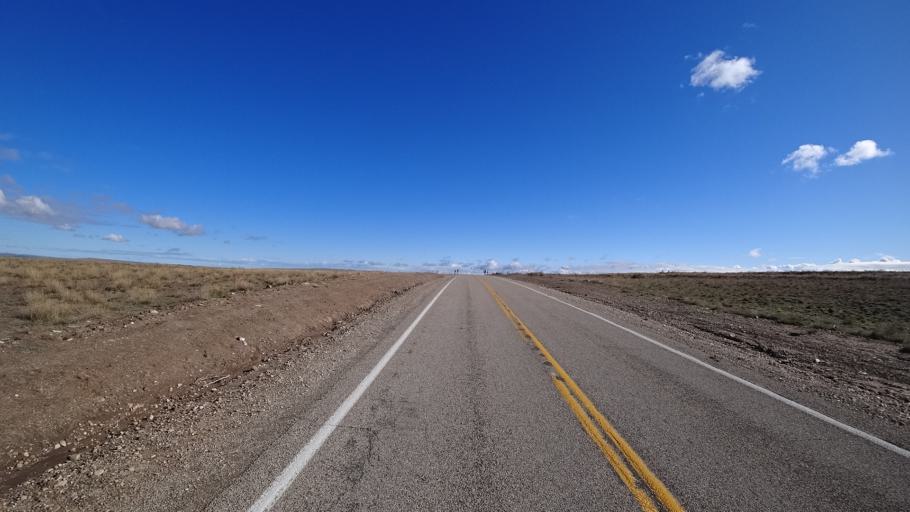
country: US
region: Idaho
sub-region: Ada County
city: Kuna
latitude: 43.3710
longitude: -116.4140
